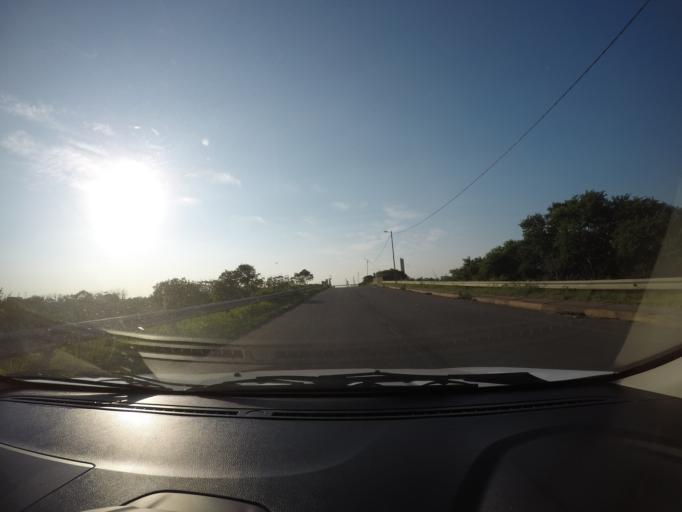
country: ZA
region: KwaZulu-Natal
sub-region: uThungulu District Municipality
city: Richards Bay
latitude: -28.7665
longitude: 32.0022
